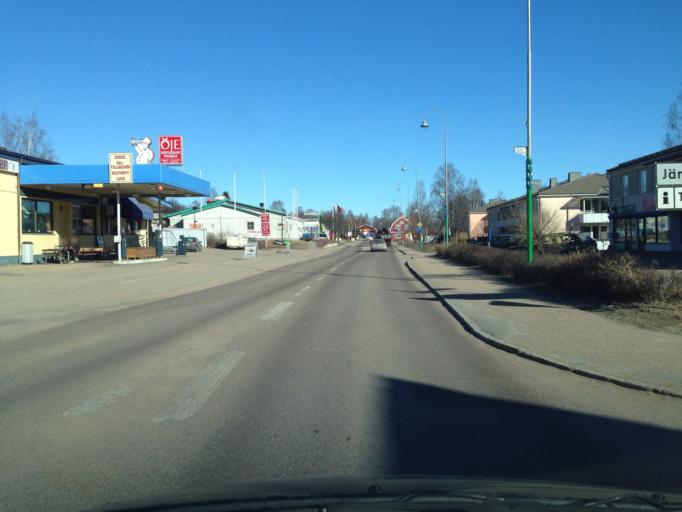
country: SE
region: Gaevleborg
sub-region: Ljusdals Kommun
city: Jaervsoe
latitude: 61.7159
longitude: 16.1697
